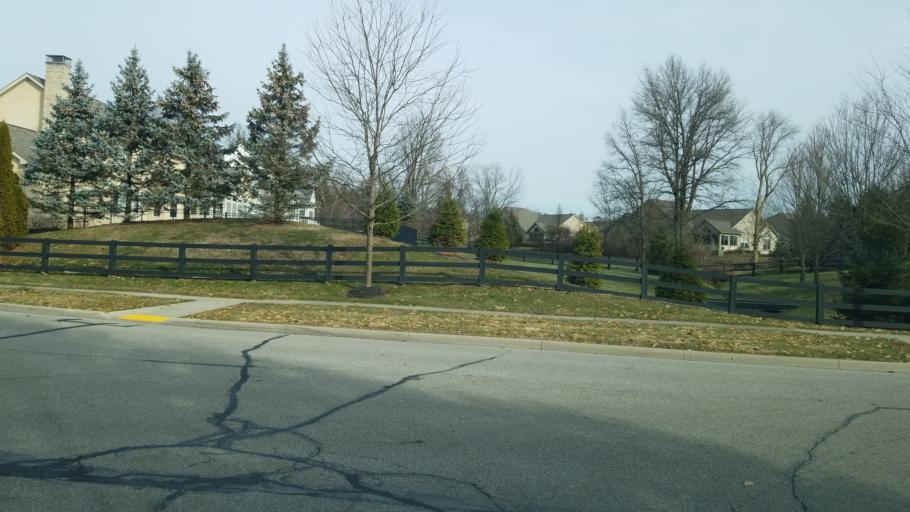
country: US
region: Ohio
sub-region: Delaware County
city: Lewis Center
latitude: 40.1673
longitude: -83.0289
